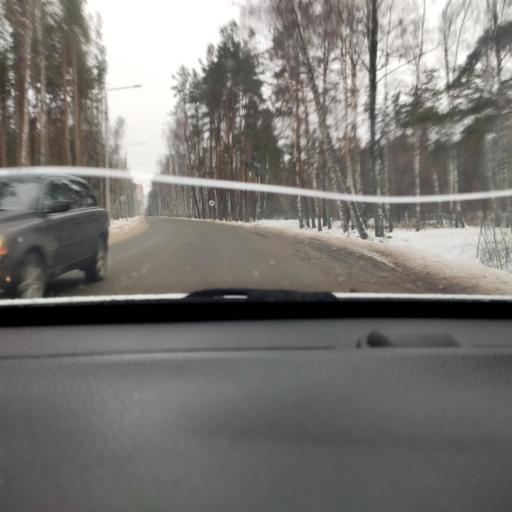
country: RU
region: Voronezj
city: Somovo
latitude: 51.7007
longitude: 39.2824
